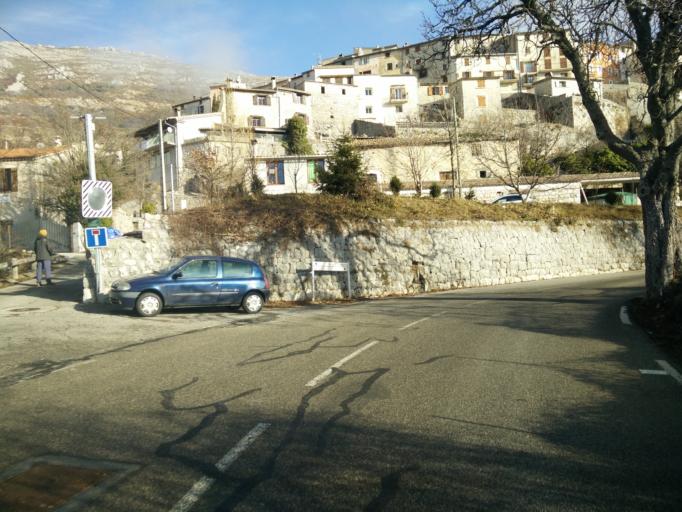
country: FR
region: Provence-Alpes-Cote d'Azur
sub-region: Departement des Alpes-Maritimes
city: Tourrettes-sur-Loup
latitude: 43.7937
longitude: 7.0380
